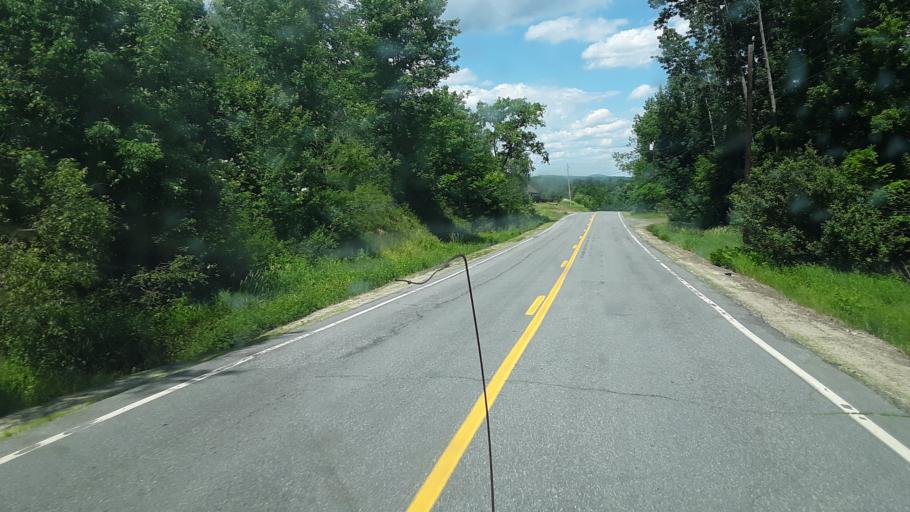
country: US
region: Maine
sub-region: Franklin County
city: Chesterville
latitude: 44.5826
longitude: -70.1534
